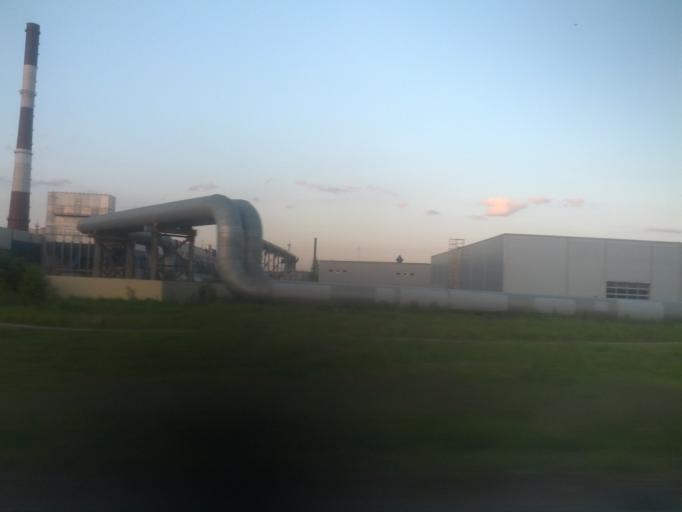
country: RU
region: St.-Petersburg
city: Staraya Derevnya
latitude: 59.9933
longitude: 30.2329
